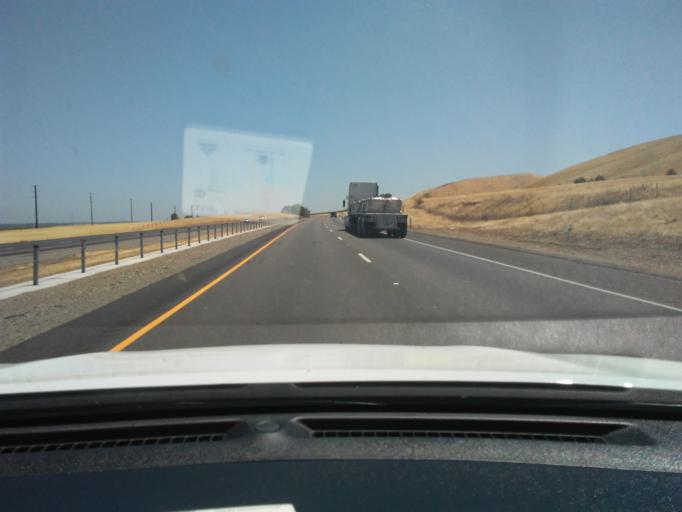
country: US
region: California
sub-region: Stanislaus County
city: Patterson
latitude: 37.4957
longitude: -121.2134
